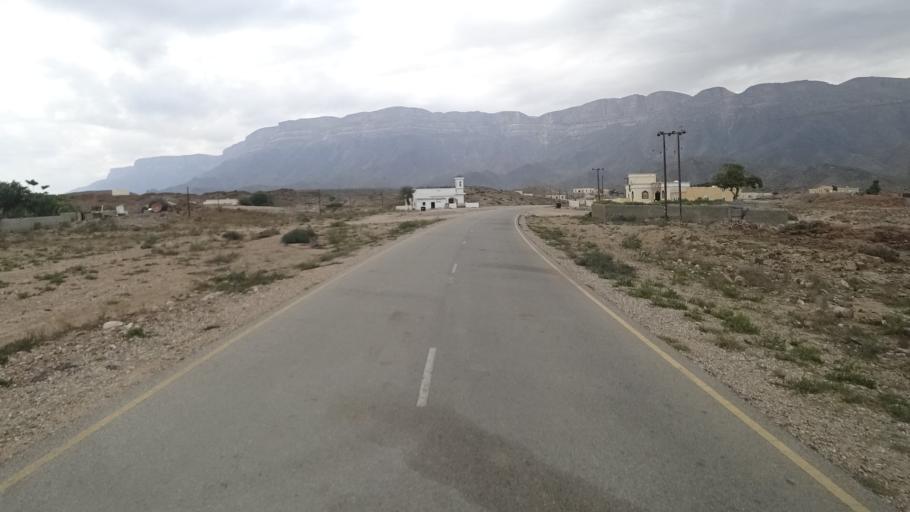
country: OM
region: Zufar
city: Salalah
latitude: 17.1632
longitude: 54.9832
